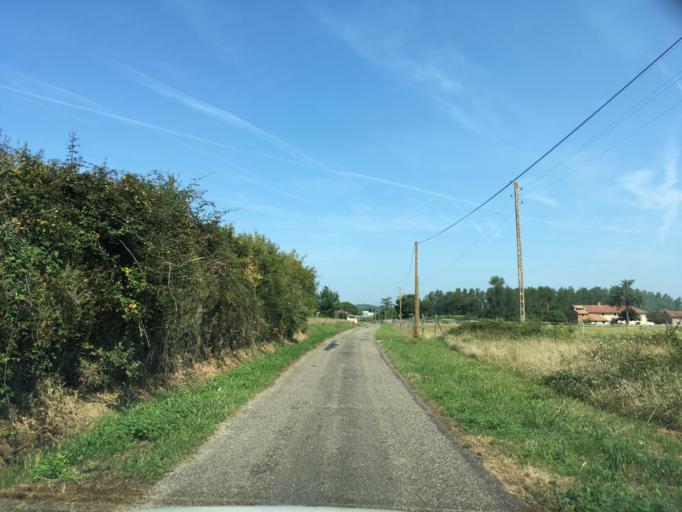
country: FR
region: Midi-Pyrenees
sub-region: Departement du Tarn-et-Garonne
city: Albias
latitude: 44.0630
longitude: 1.4202
